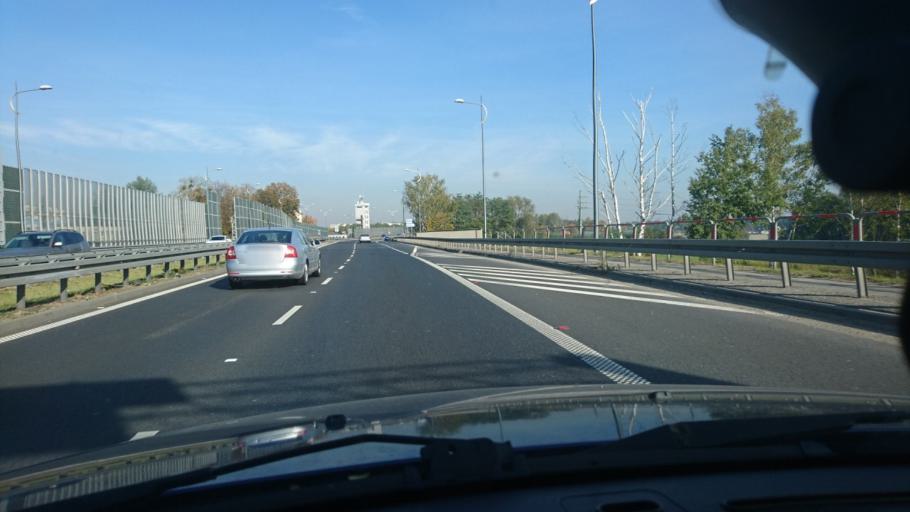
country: PL
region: Silesian Voivodeship
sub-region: Tychy
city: Cielmice
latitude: 50.1065
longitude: 19.0077
